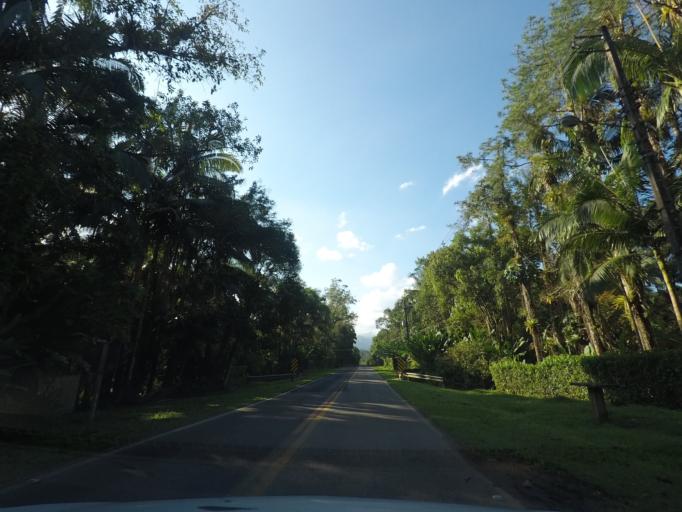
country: BR
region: Parana
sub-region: Antonina
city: Antonina
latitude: -25.4160
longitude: -48.8738
